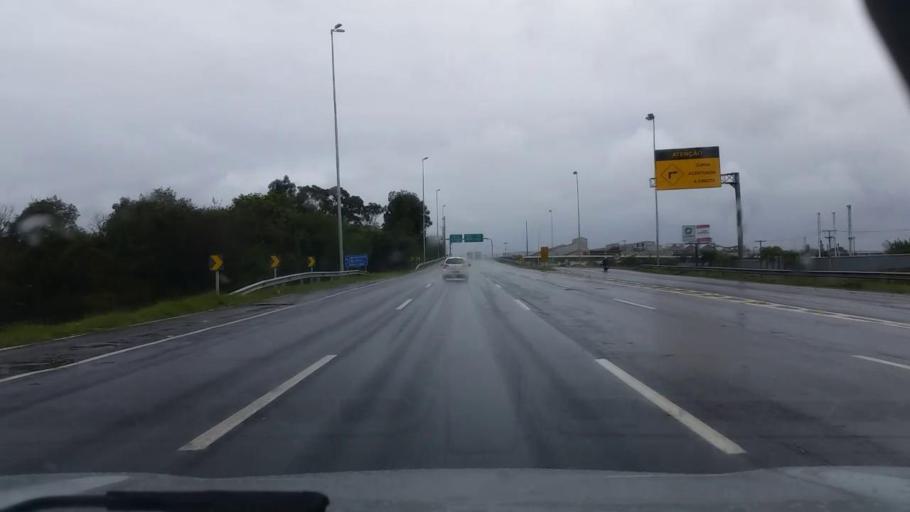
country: BR
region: Rio Grande do Sul
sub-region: Canoas
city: Canoas
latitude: -29.9692
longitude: -51.1723
